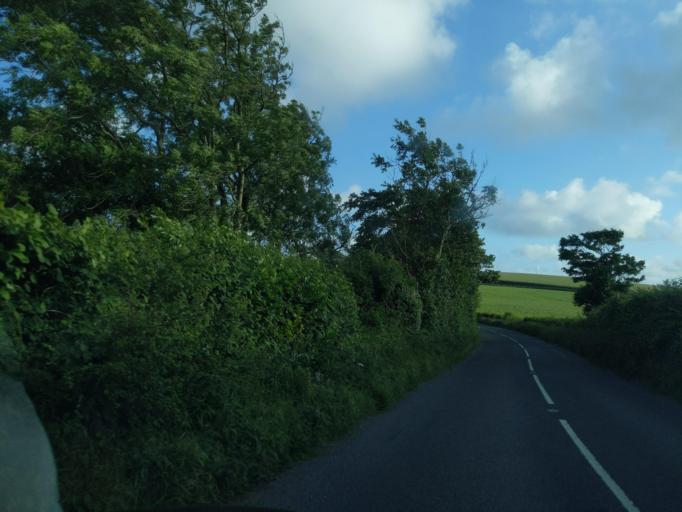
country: GB
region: England
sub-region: Devon
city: Fremington
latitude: 51.0112
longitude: -4.1097
